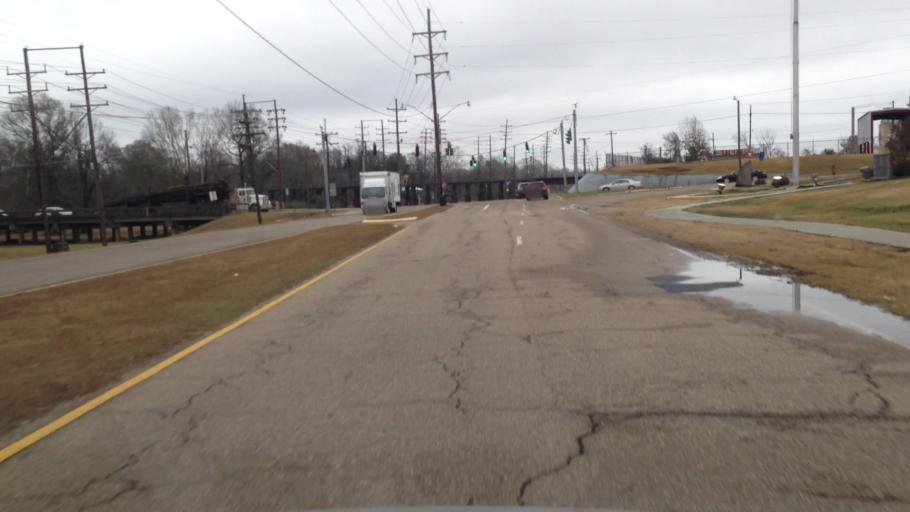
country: US
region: Louisiana
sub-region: Washington Parish
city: Bogalusa
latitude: 30.7824
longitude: -89.8662
